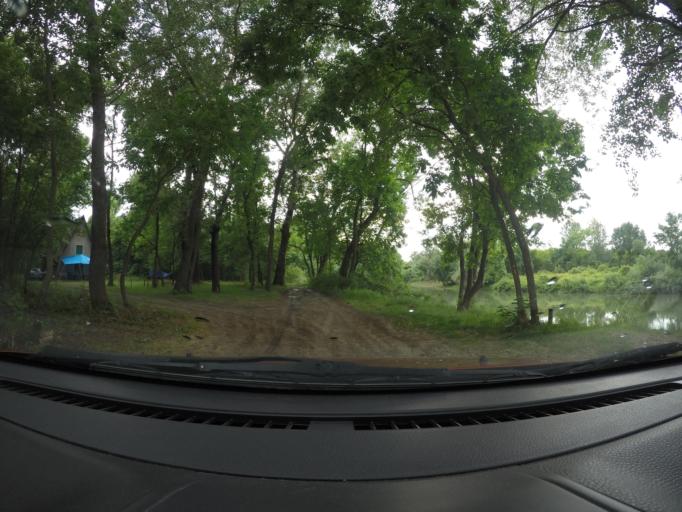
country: RS
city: Orlovat
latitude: 45.2097
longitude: 20.5741
